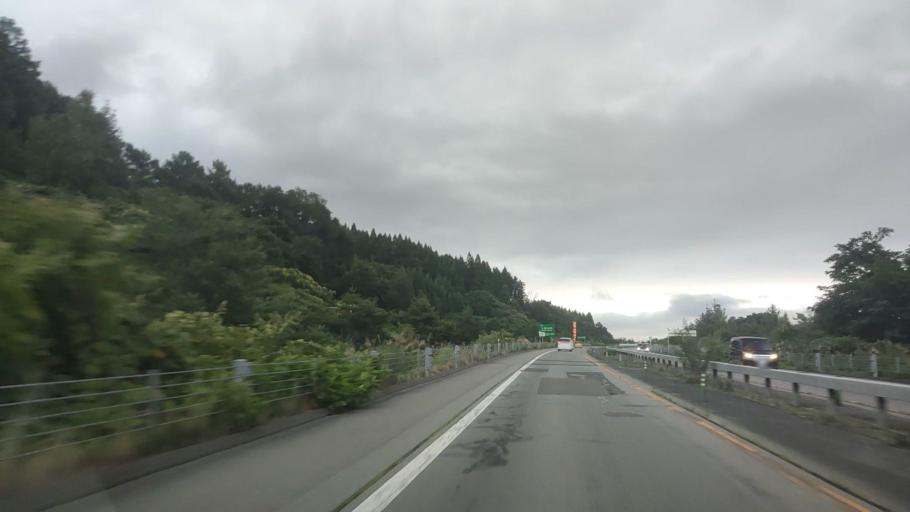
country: JP
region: Hokkaido
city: Nanae
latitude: 41.9089
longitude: 140.6951
